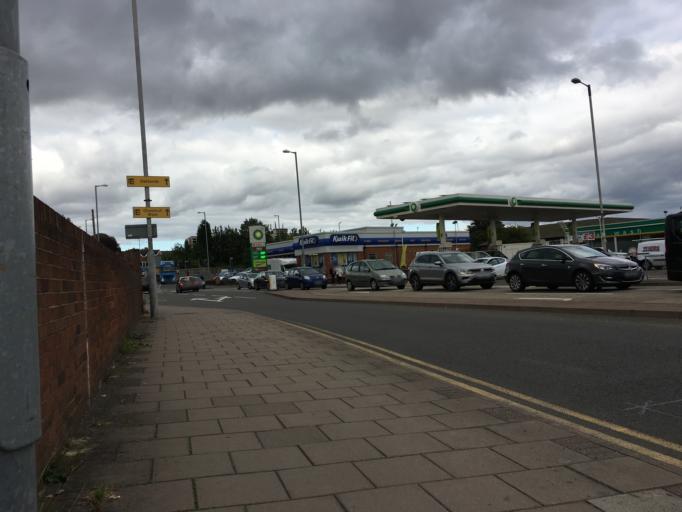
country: GB
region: England
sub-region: Staffordshire
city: Tamworth
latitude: 52.6365
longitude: -1.6949
